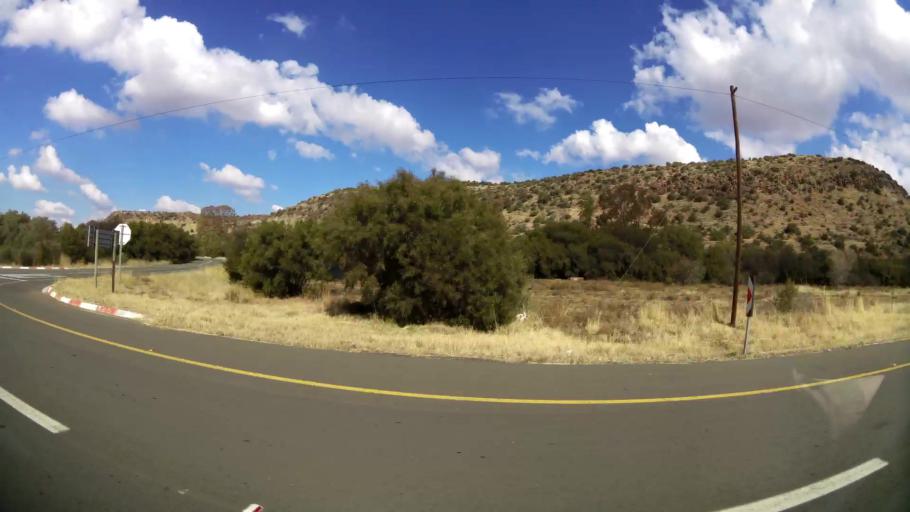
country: ZA
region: Orange Free State
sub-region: Mangaung Metropolitan Municipality
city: Bloemfontein
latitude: -29.1591
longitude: 26.0493
